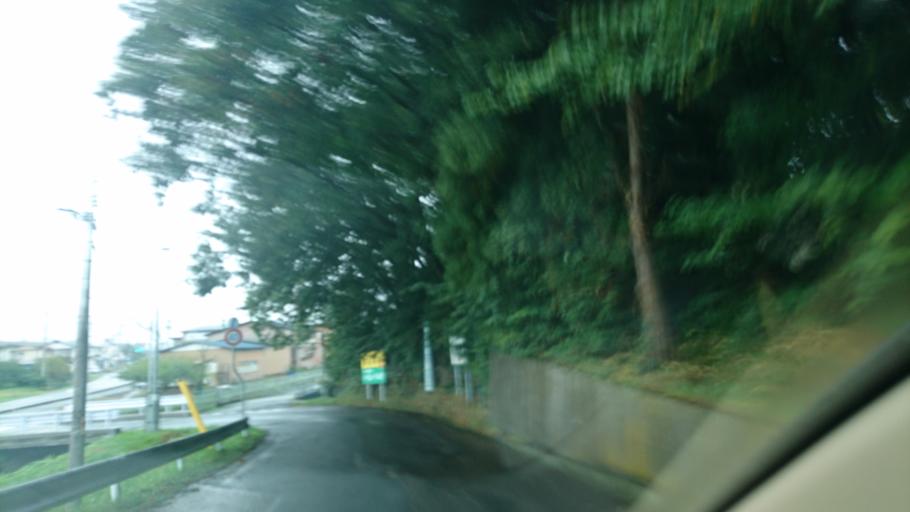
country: JP
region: Iwate
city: Mizusawa
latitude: 39.1352
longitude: 141.1870
